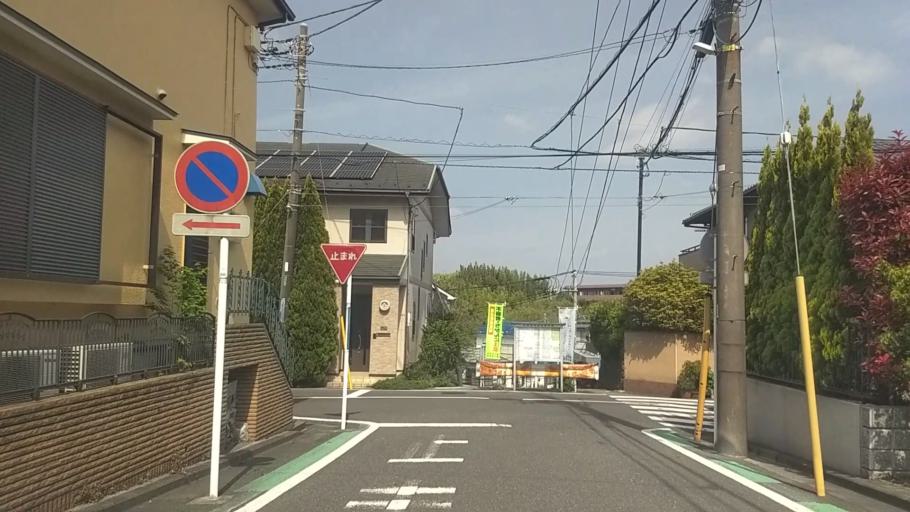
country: JP
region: Kanagawa
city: Yokohama
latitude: 35.3729
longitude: 139.6135
